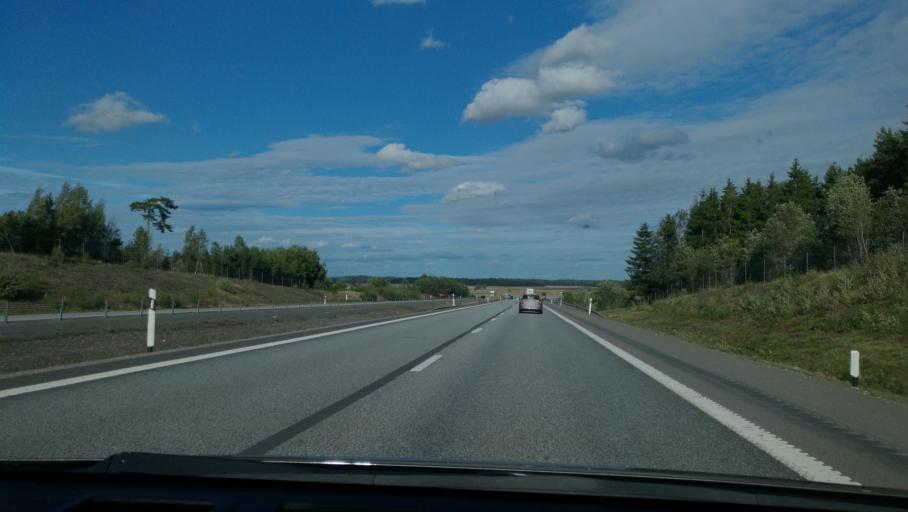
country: SE
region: OErebro
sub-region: Lekebergs Kommun
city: Fjugesta
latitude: 59.0256
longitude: 14.8139
